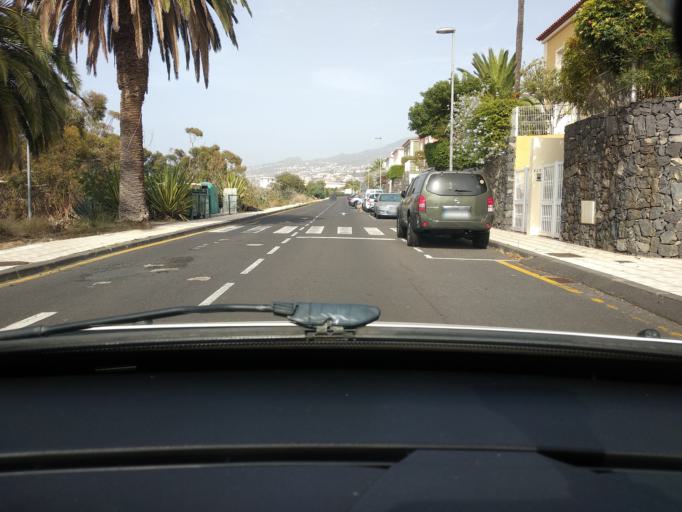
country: ES
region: Canary Islands
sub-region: Provincia de Santa Cruz de Tenerife
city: Santa Ursula
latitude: 28.4281
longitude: -16.4935
